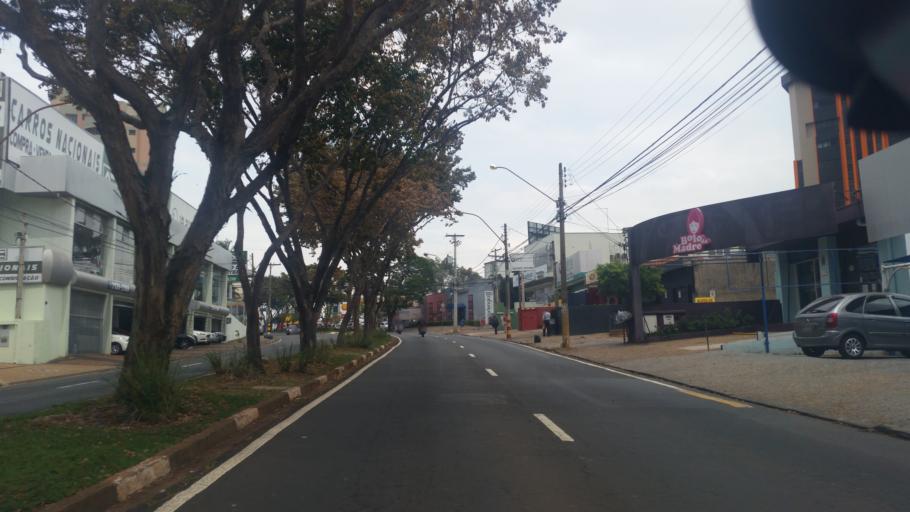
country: BR
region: Sao Paulo
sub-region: Campinas
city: Campinas
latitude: -22.8880
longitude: -47.0763
